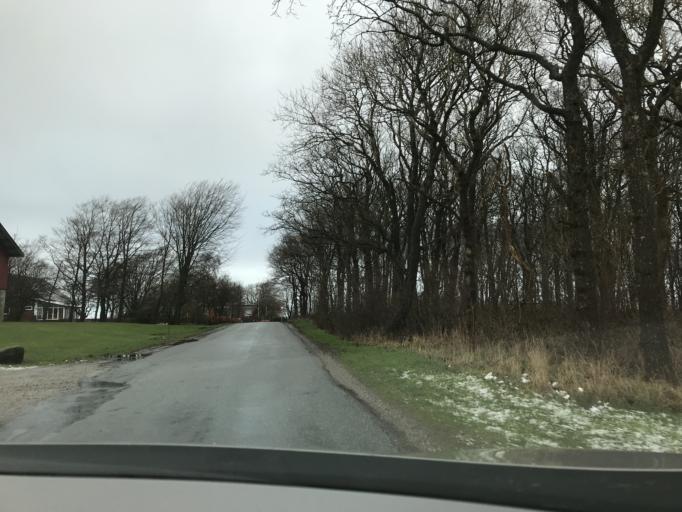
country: DK
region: South Denmark
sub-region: Varde Kommune
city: Varde
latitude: 55.6582
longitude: 8.4190
